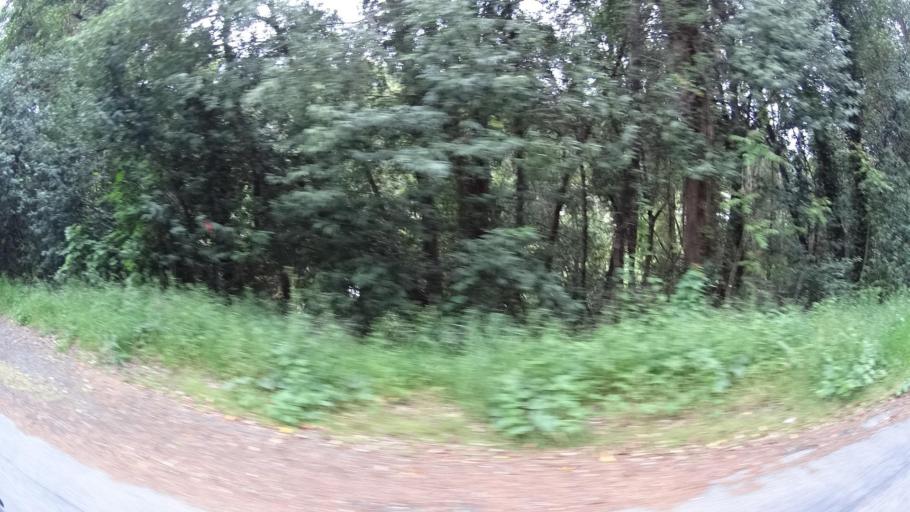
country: US
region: California
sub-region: Humboldt County
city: Willow Creek
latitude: 40.9663
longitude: -123.6345
